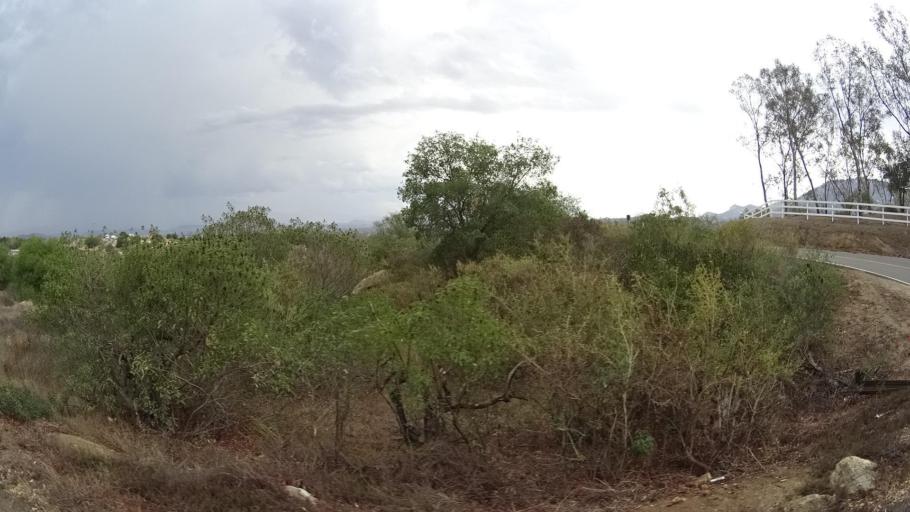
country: US
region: California
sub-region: San Diego County
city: San Pasqual
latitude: 33.0388
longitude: -116.9713
